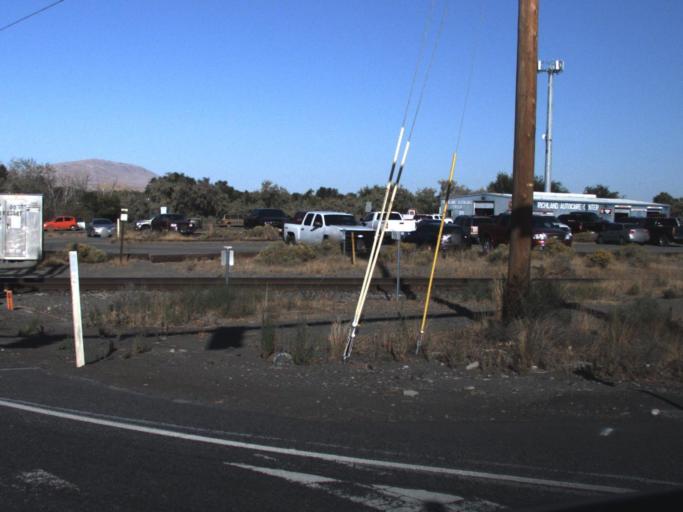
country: US
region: Washington
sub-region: Benton County
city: Richland
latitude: 46.2931
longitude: -119.3051
